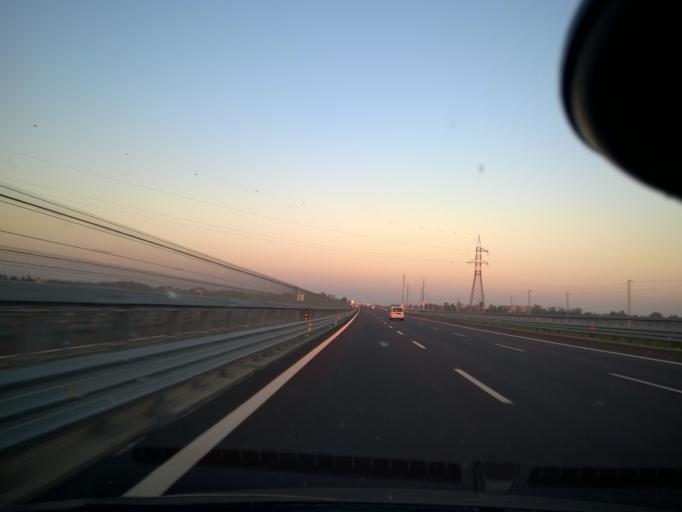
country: IT
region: Lombardy
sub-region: Provincia di Brescia
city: Urago d'Oglio
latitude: 45.5000
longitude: 9.8683
